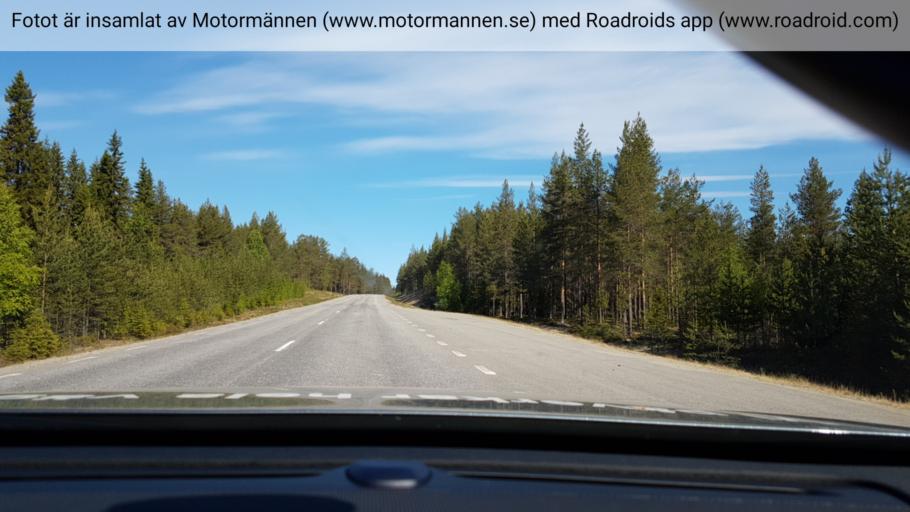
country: SE
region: Vaesterbotten
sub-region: Bjurholms Kommun
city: Bjurholm
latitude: 63.9915
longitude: 18.7968
